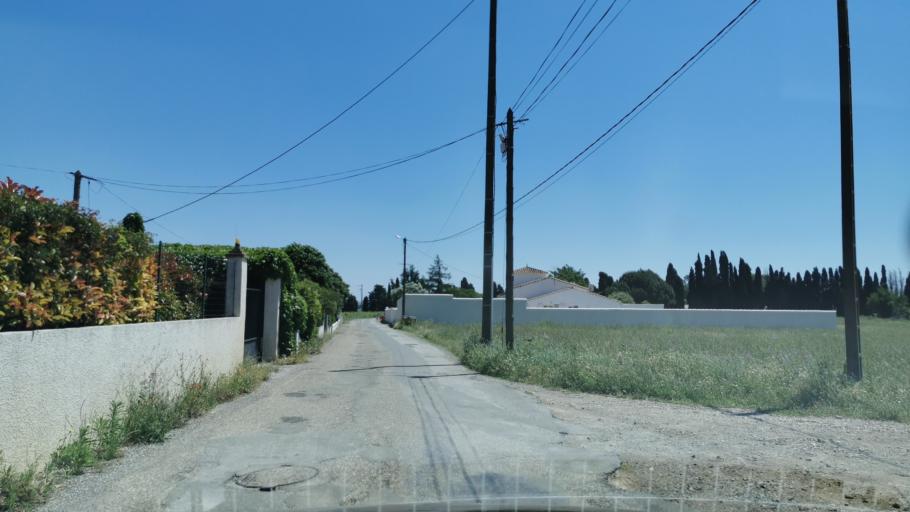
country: FR
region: Languedoc-Roussillon
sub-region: Departement de l'Aude
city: Saint-Marcel-sur-Aude
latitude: 43.2642
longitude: 2.9521
